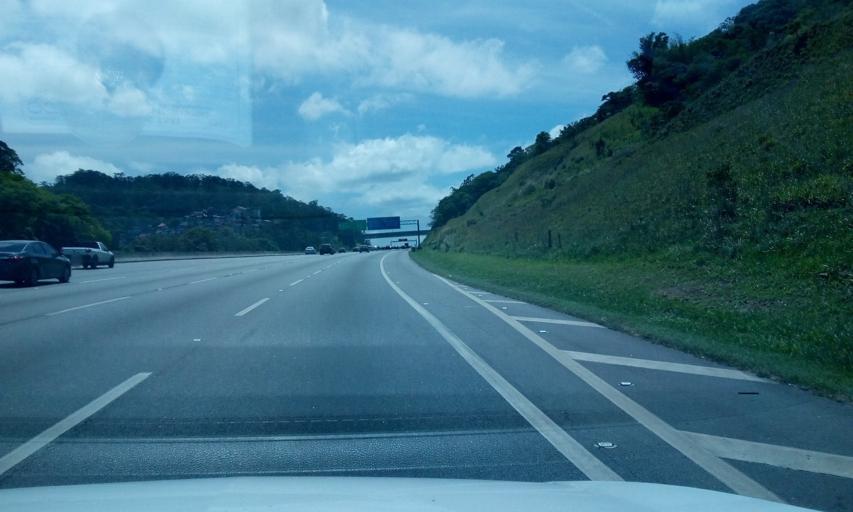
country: BR
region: Sao Paulo
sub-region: Osasco
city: Osasco
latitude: -23.4630
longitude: -46.7518
